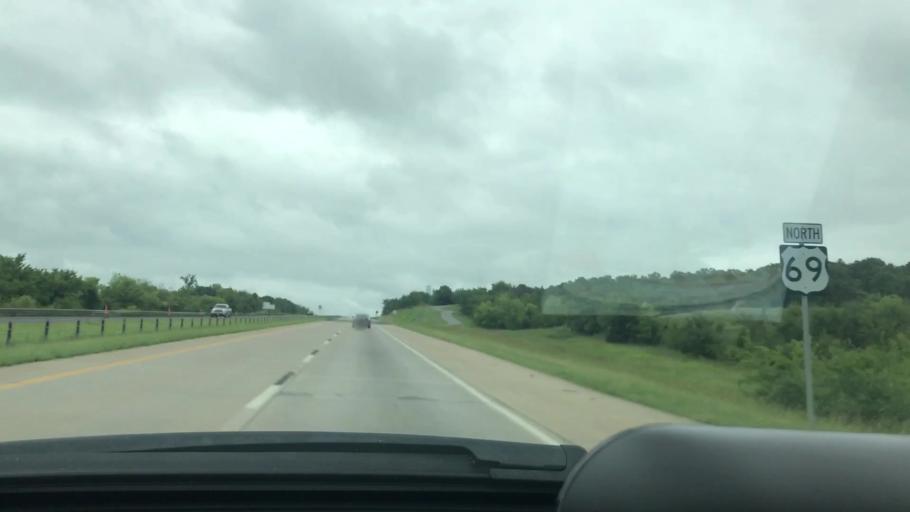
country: US
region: Oklahoma
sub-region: Pittsburg County
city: Krebs
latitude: 34.9640
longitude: -95.7244
